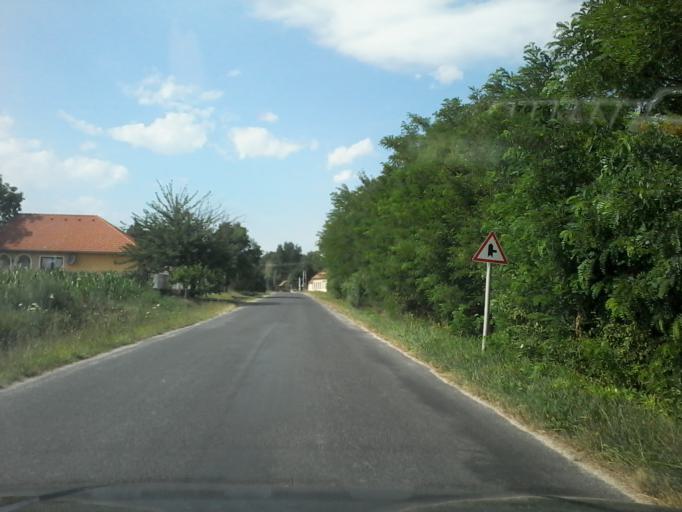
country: HU
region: Vas
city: Celldomolk
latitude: 47.2060
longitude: 17.1063
